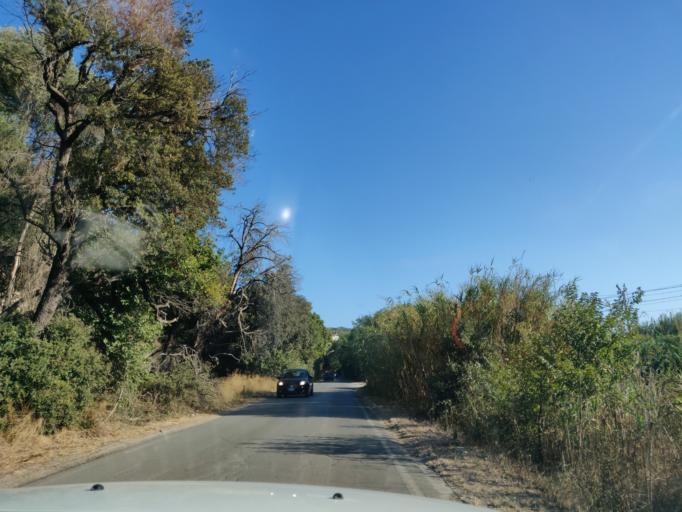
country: IT
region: Tuscany
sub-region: Provincia di Grosseto
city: Orbetello Scalo
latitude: 42.4225
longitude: 11.2819
